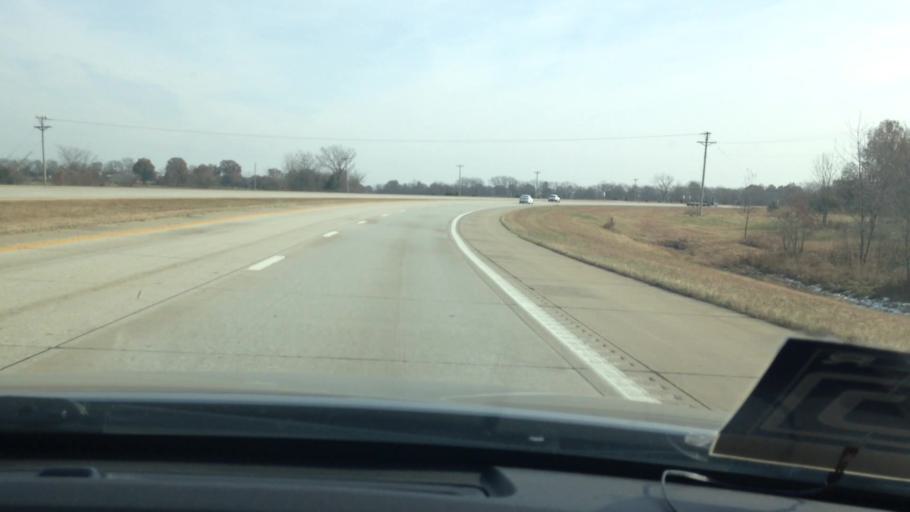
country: US
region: Missouri
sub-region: Henry County
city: Clinton
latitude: 38.4637
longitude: -93.9739
